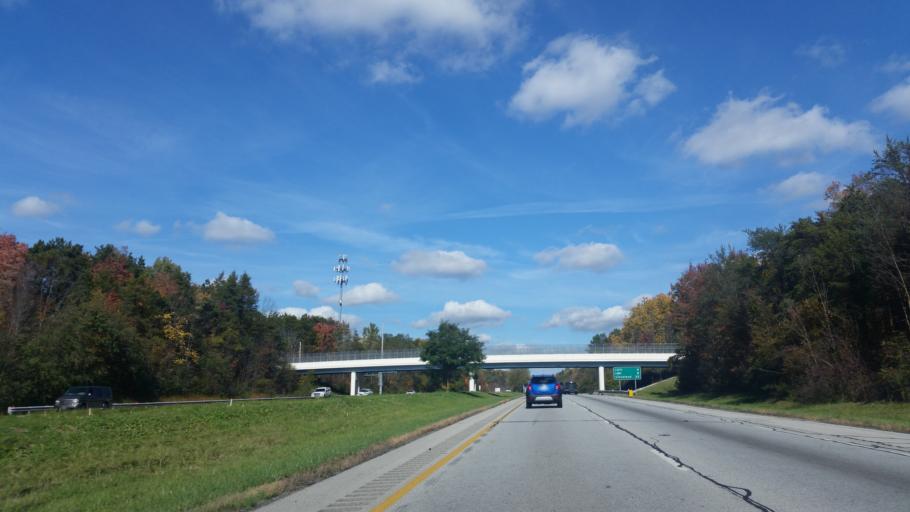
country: US
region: Ohio
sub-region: Summit County
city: Montrose-Ghent
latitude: 41.1620
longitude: -81.6260
